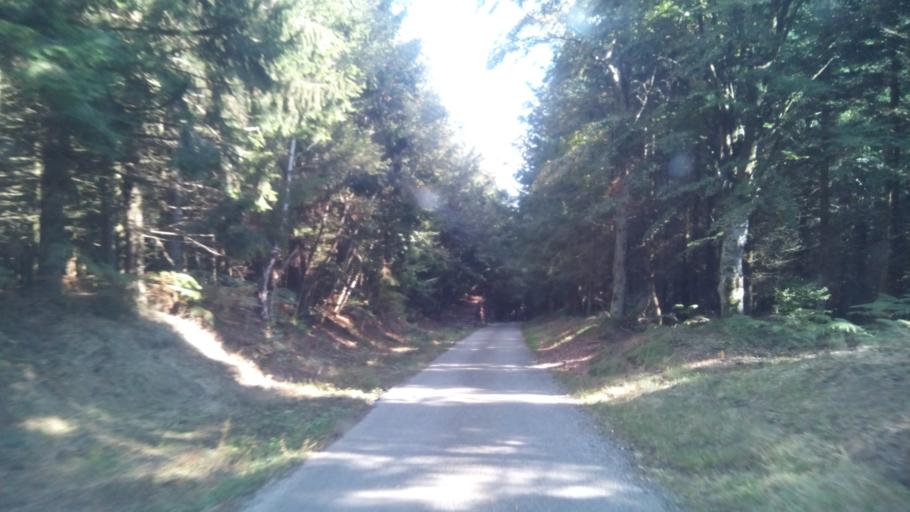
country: FR
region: Rhone-Alpes
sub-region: Departement du Rhone
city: Beaujeu
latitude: 46.1995
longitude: 4.4981
